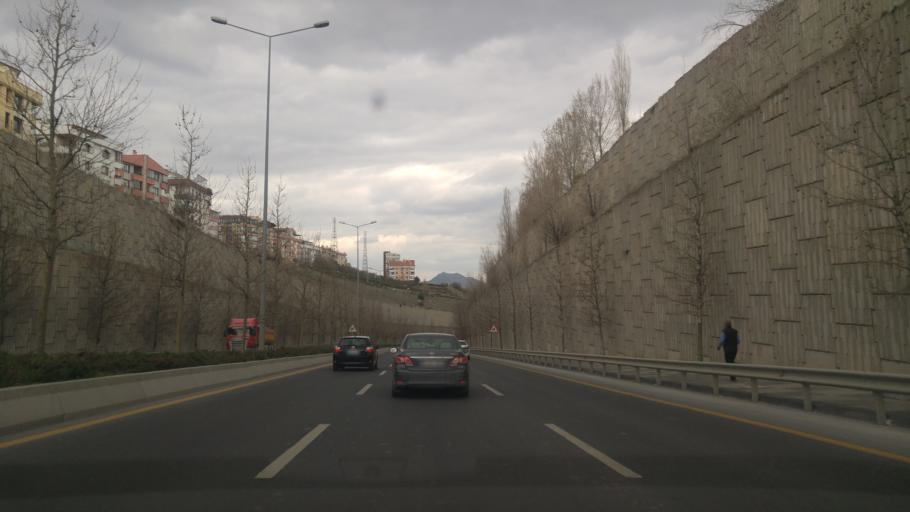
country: TR
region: Ankara
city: Cankaya
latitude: 39.8843
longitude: 32.8888
